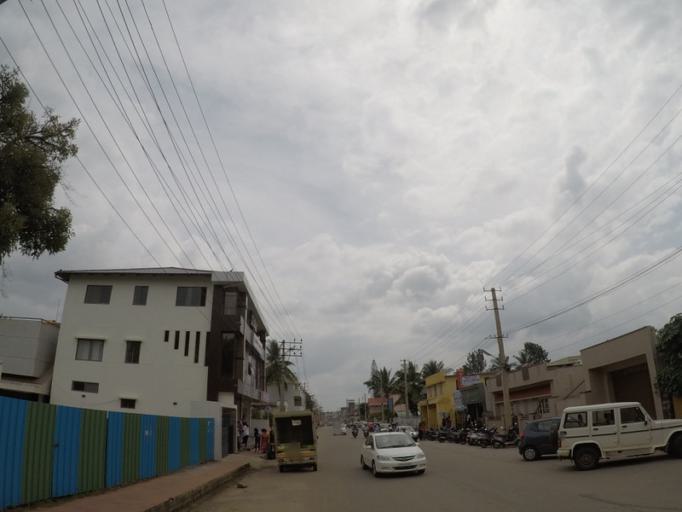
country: IN
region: Karnataka
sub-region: Chikmagalur
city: Chikmagalur
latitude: 13.3290
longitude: 75.7728
